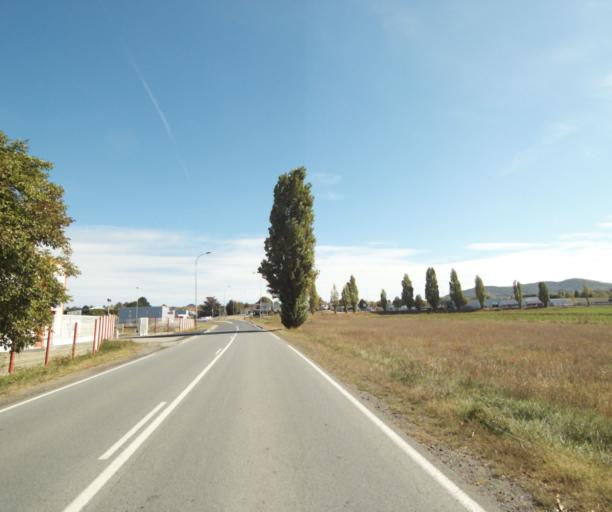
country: FR
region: Auvergne
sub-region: Departement du Puy-de-Dome
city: Pont-du-Chateau
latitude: 45.7934
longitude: 3.2250
